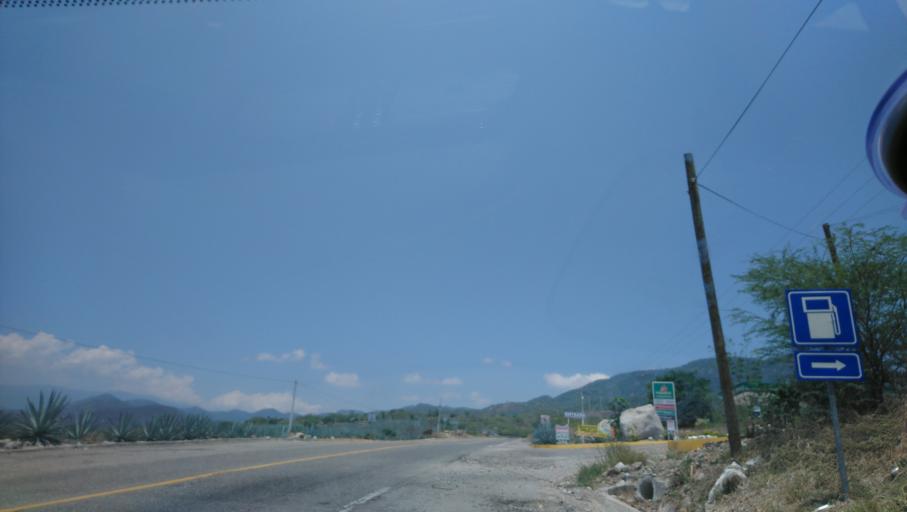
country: MX
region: Oaxaca
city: San Carlos Yautepec
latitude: 16.5624
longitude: -96.0208
